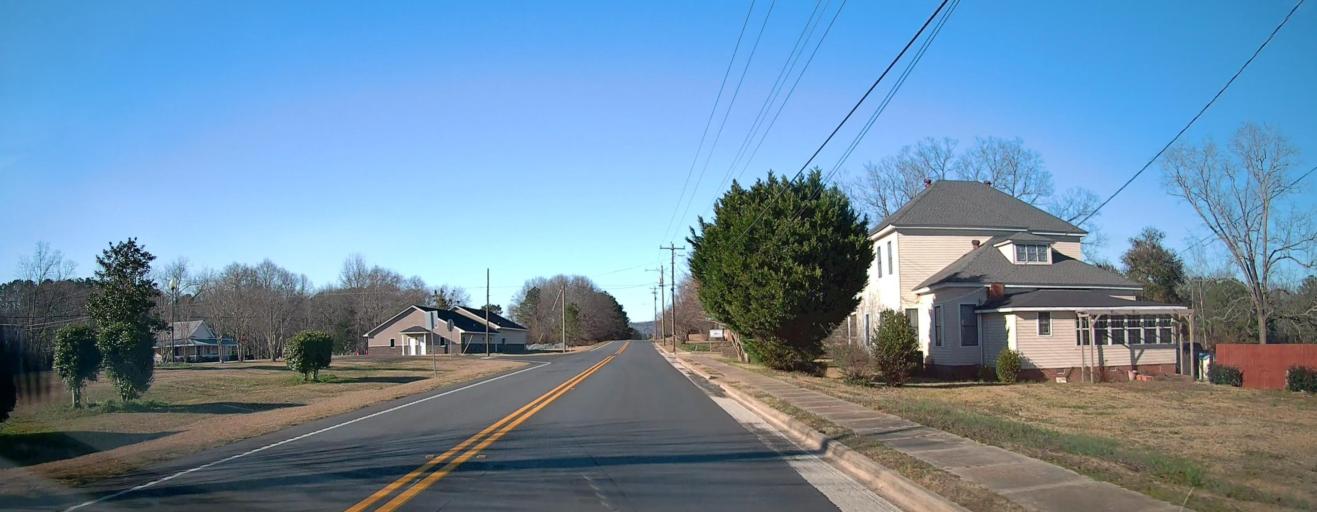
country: US
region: Georgia
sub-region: Talbot County
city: Sardis
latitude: 32.8094
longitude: -84.6964
